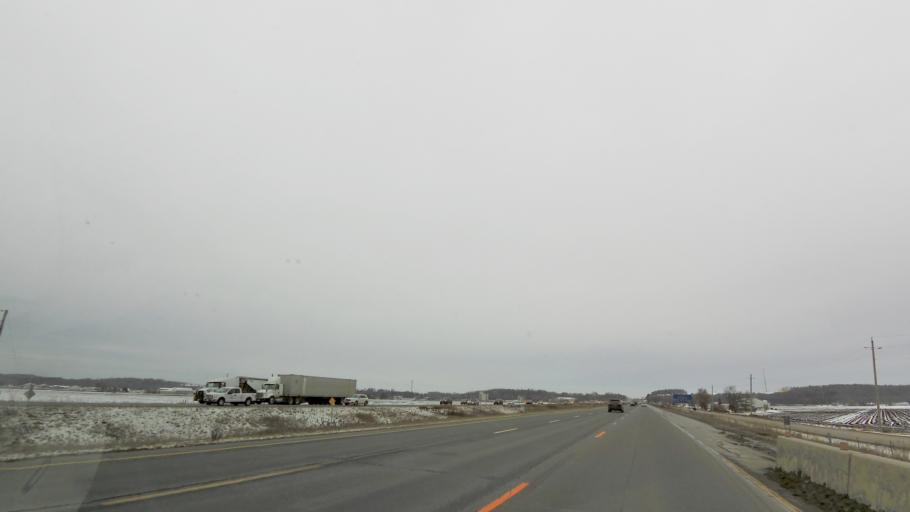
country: CA
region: Ontario
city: Bradford West Gwillimbury
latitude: 44.0415
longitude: -79.5996
